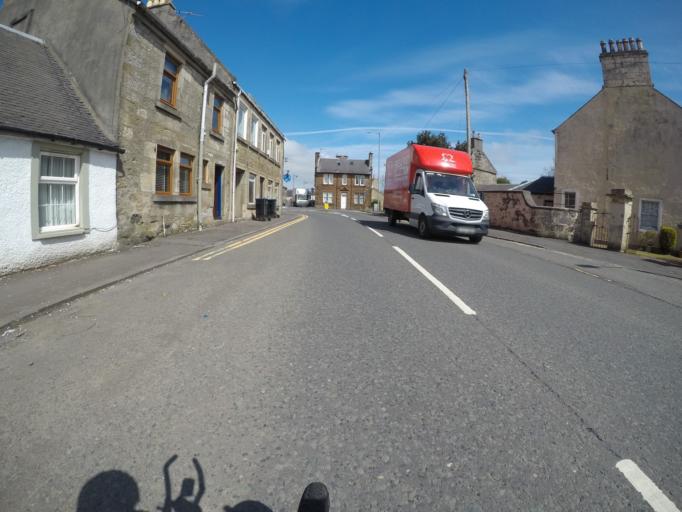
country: GB
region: Scotland
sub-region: East Ayrshire
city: Stewarton
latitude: 55.6788
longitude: -4.5180
